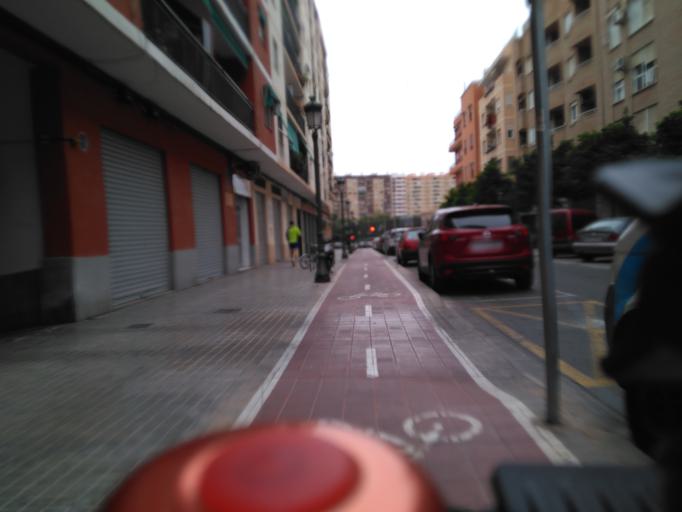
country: ES
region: Valencia
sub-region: Provincia de Valencia
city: Mislata
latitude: 39.4730
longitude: -0.3989
